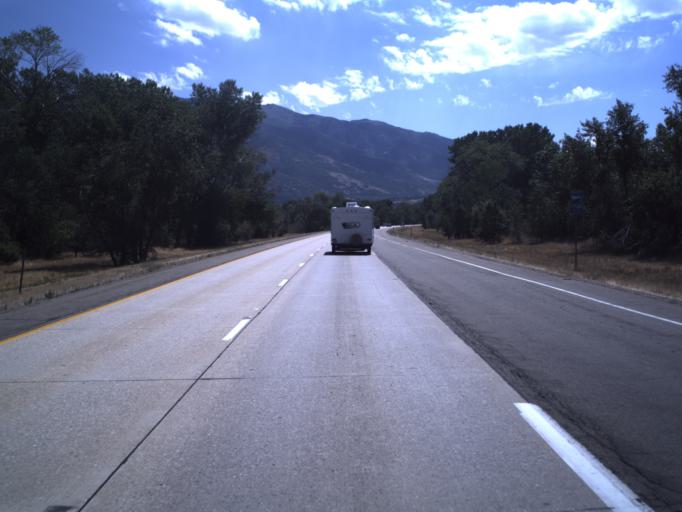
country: US
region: Utah
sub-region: Weber County
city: Washington Terrace
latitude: 41.1460
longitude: -111.9620
